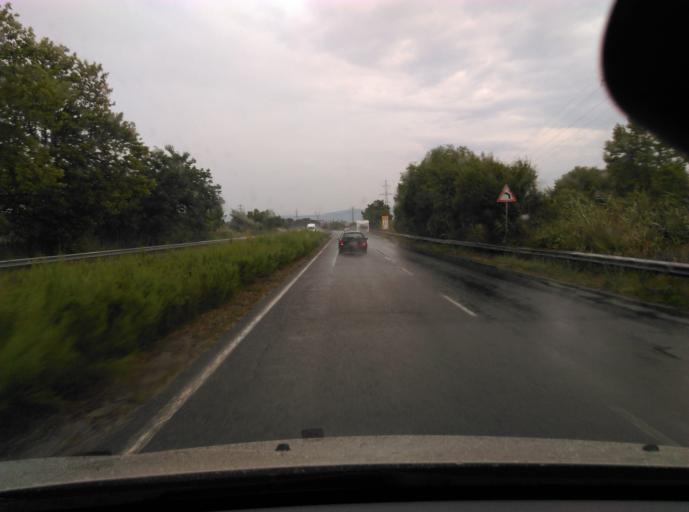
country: BG
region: Burgas
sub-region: Obshtina Burgas
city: Burgas
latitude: 42.4452
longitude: 27.4610
